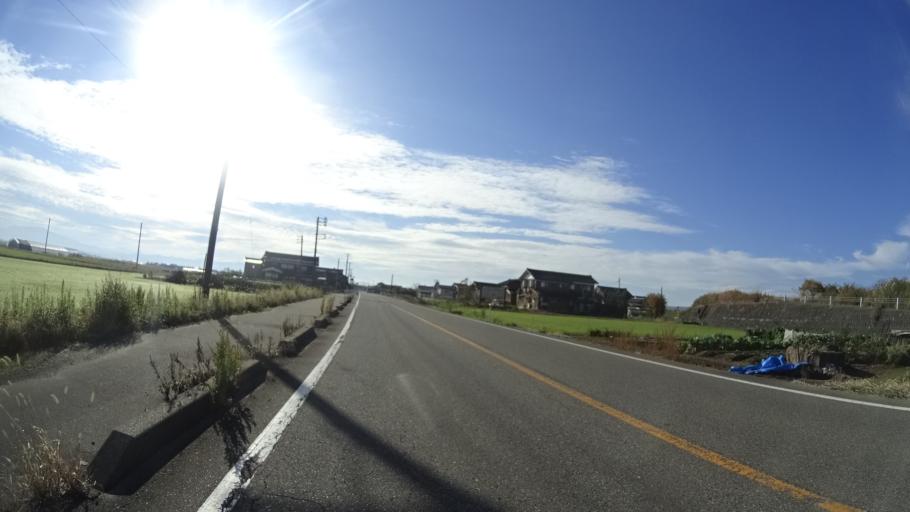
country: JP
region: Niigata
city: Mitsuke
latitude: 37.5813
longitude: 138.8345
